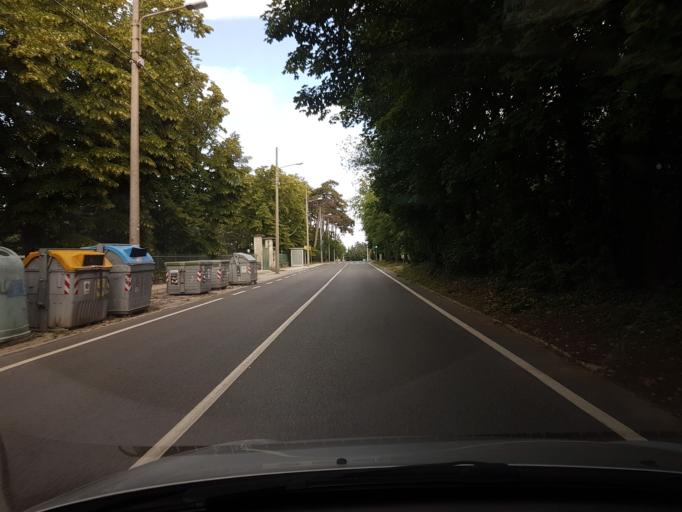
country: IT
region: Friuli Venezia Giulia
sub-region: Provincia di Trieste
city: Villa Opicina
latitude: 45.6816
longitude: 13.8031
